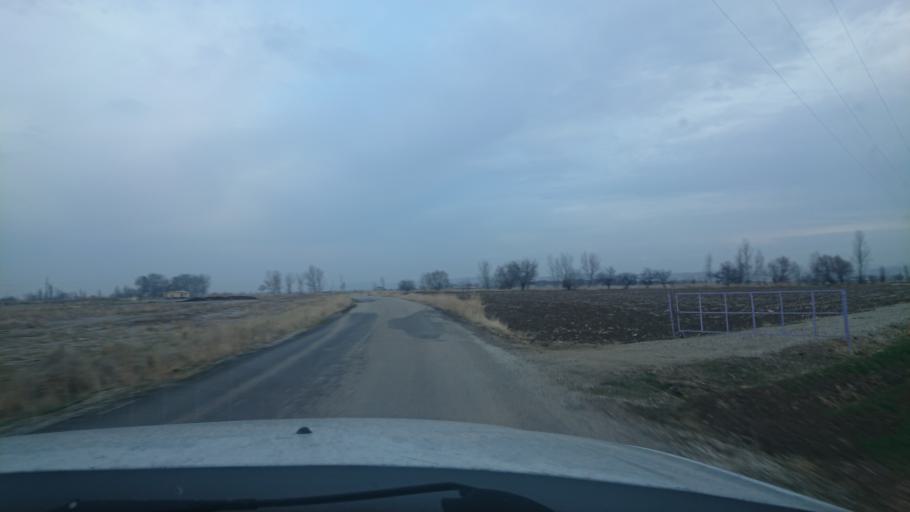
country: TR
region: Aksaray
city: Yesilova
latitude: 38.4440
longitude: 33.8369
